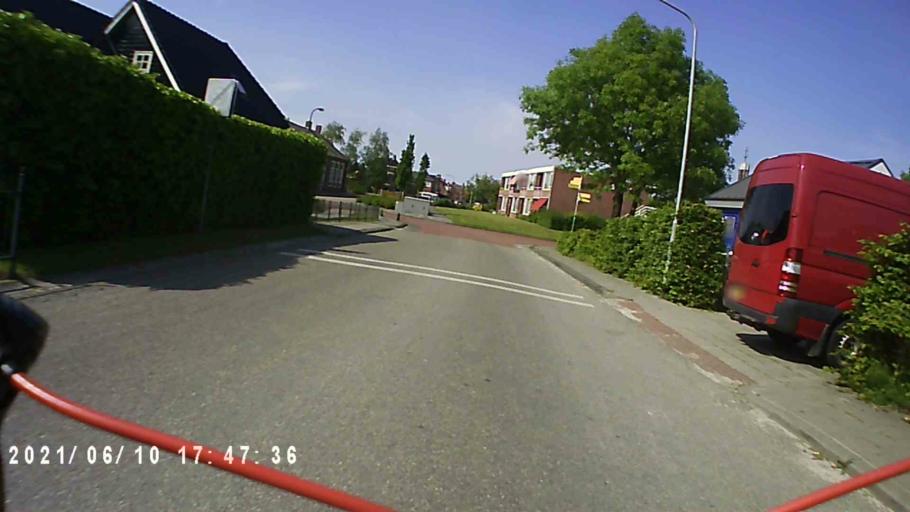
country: NL
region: Groningen
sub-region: Gemeente De Marne
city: Ulrum
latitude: 53.3370
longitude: 6.3033
